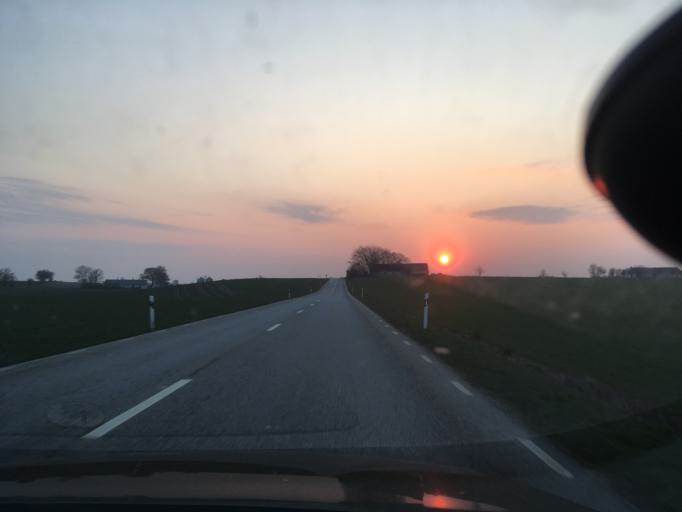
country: SE
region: Skane
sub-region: Tomelilla Kommun
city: Tomelilla
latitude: 55.4765
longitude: 14.0612
